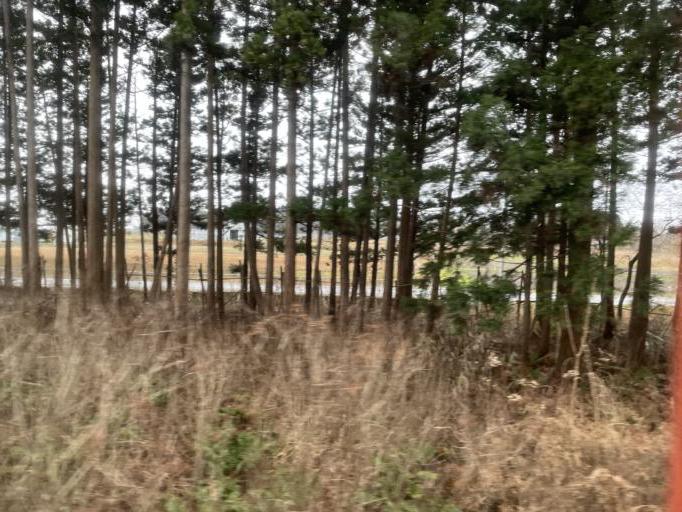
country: JP
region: Aomori
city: Aomori Shi
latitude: 40.9842
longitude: 140.6534
